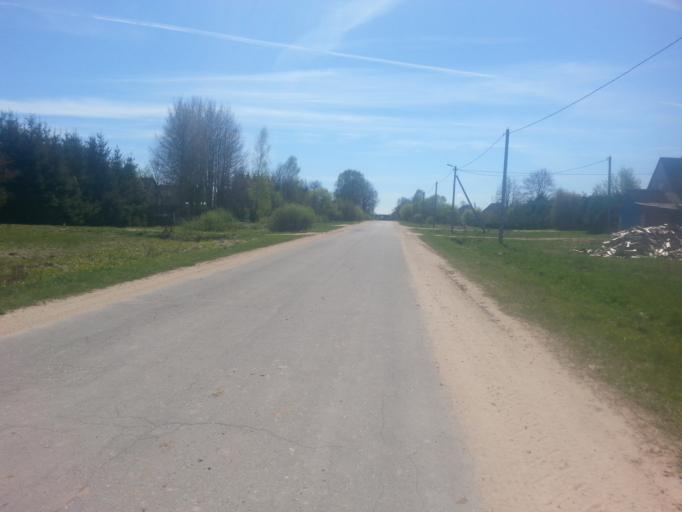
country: BY
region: Minsk
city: Narach
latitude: 54.9445
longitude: 26.6953
